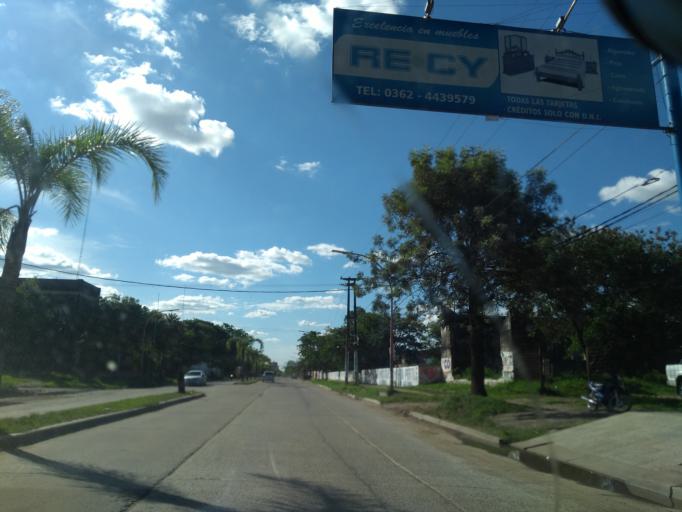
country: AR
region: Chaco
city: Barranqueras
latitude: -27.4748
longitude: -58.9598
